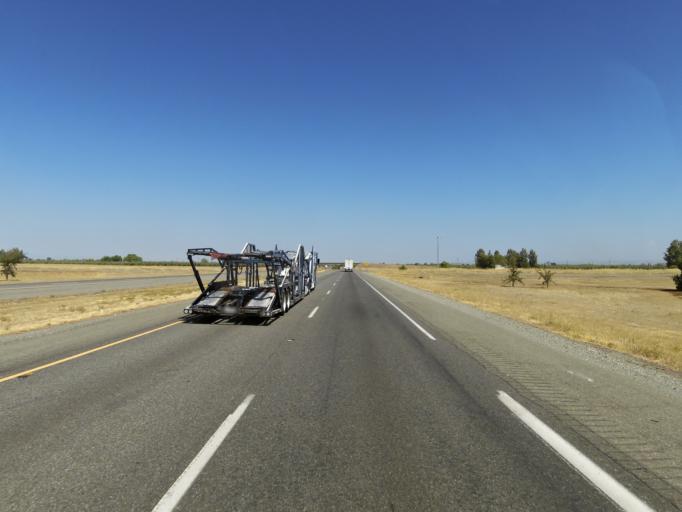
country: US
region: California
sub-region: Tehama County
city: Corning
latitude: 39.9572
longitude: -122.2001
